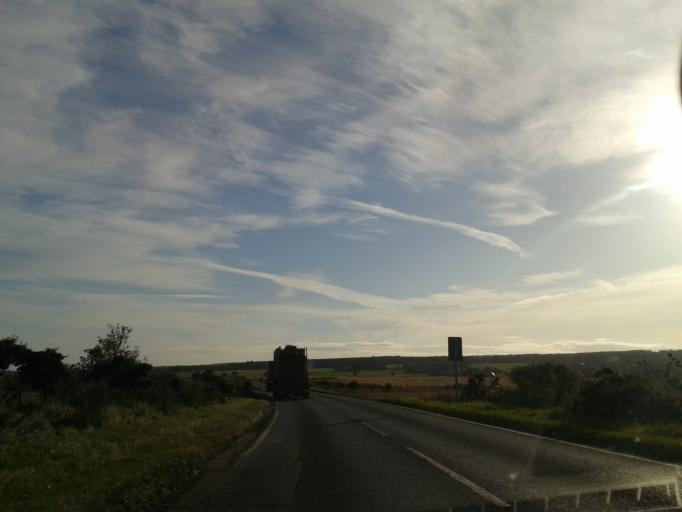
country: GB
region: Scotland
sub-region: Highland
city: Fortrose
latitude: 57.5012
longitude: -4.1359
